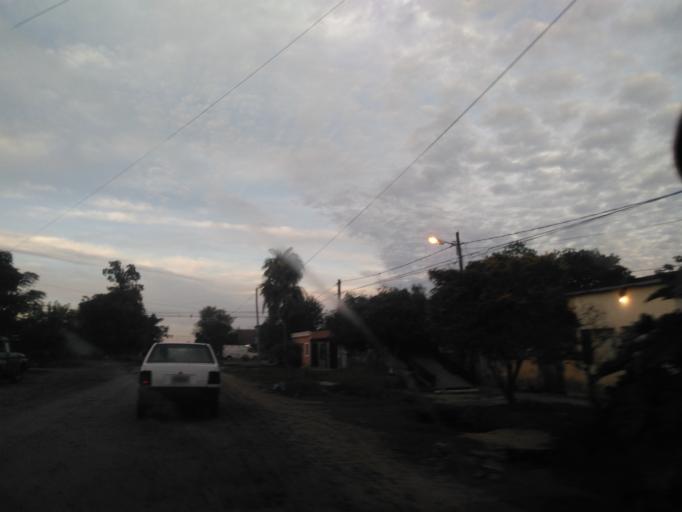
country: AR
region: Chaco
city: Resistencia
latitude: -27.4748
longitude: -58.9986
